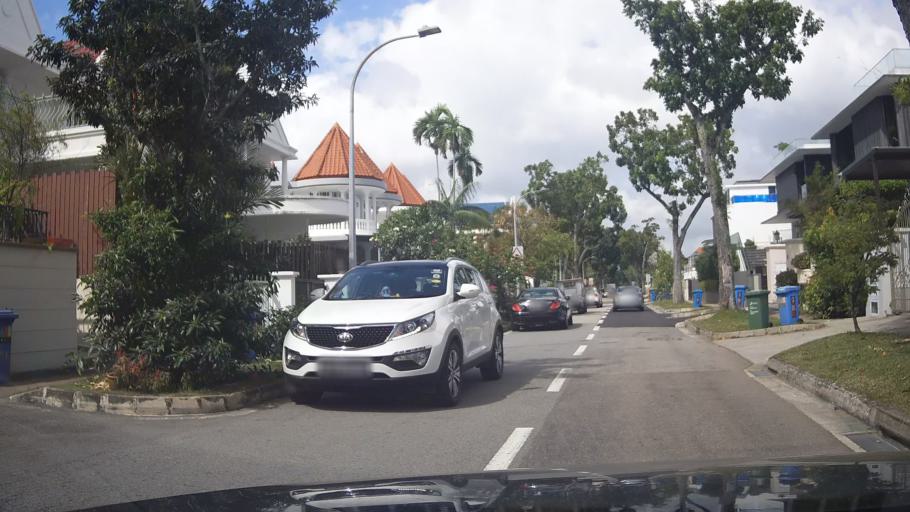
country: SG
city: Singapore
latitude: 1.3029
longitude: 103.8944
